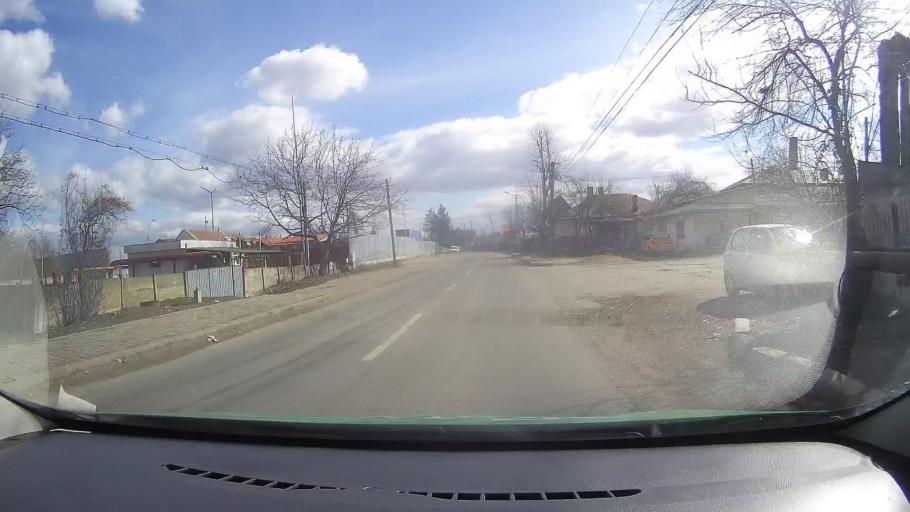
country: RO
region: Dambovita
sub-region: Municipiul Targoviste
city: Targoviste
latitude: 44.9415
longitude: 25.4402
